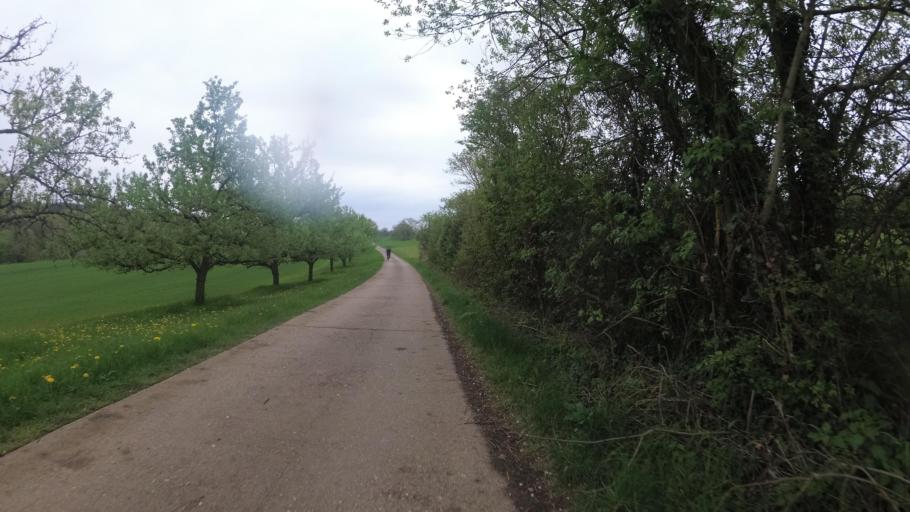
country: DE
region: Saarland
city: Rehlingen-Siersburg
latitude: 49.3376
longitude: 6.6221
